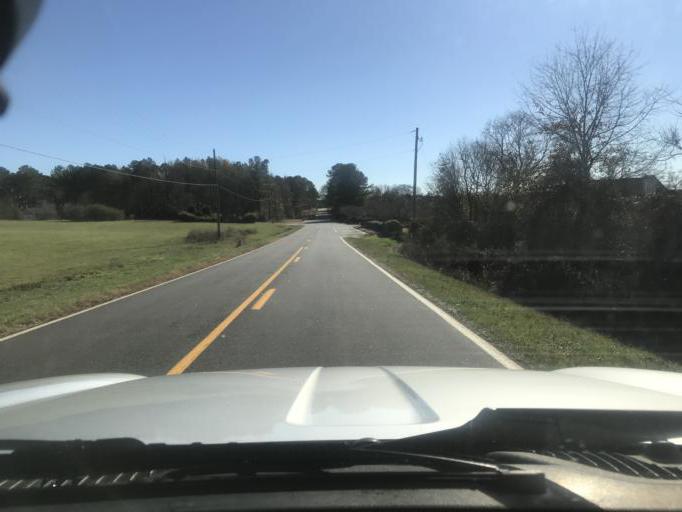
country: US
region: Georgia
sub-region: Barrow County
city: Winder
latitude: 33.9184
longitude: -83.7642
